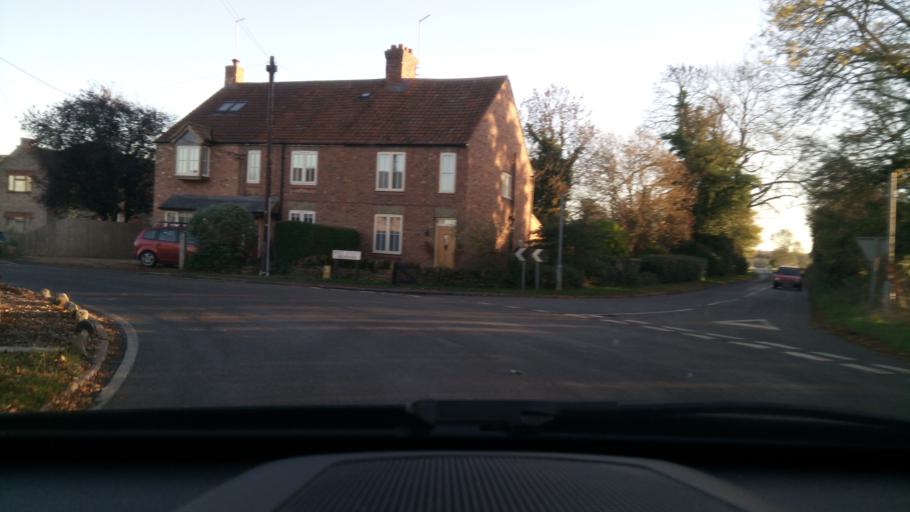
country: GB
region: England
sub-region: Peterborough
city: Helpston
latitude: 52.6352
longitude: -0.3578
